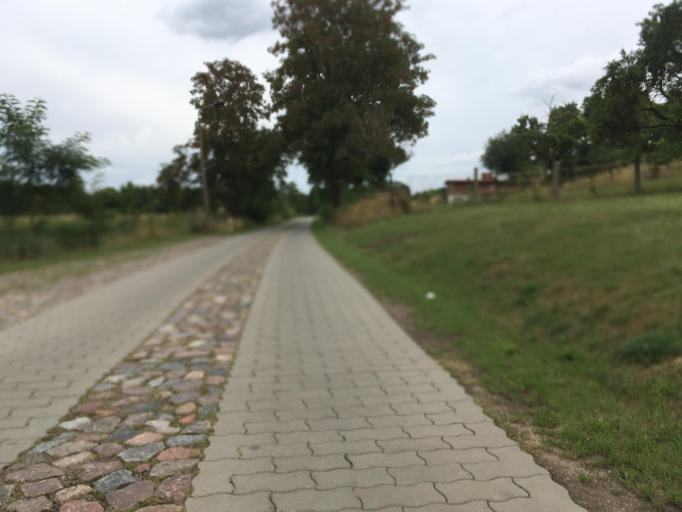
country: DE
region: Brandenburg
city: Passow
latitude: 53.1668
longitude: 14.0952
